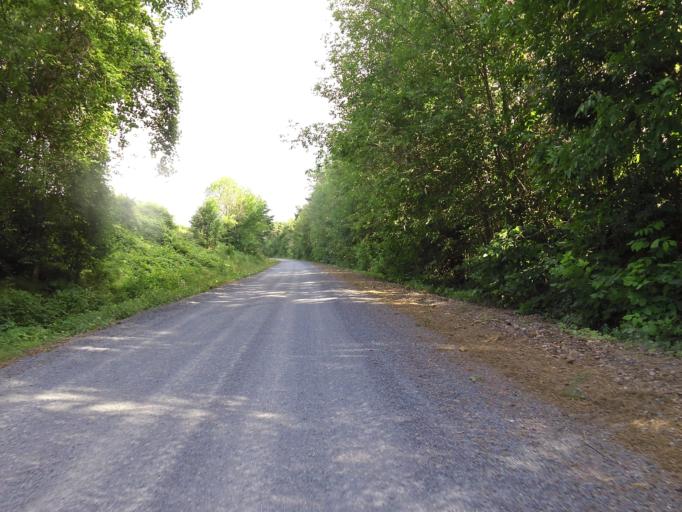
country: CA
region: Ontario
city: Arnprior
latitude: 45.3169
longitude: -76.2849
